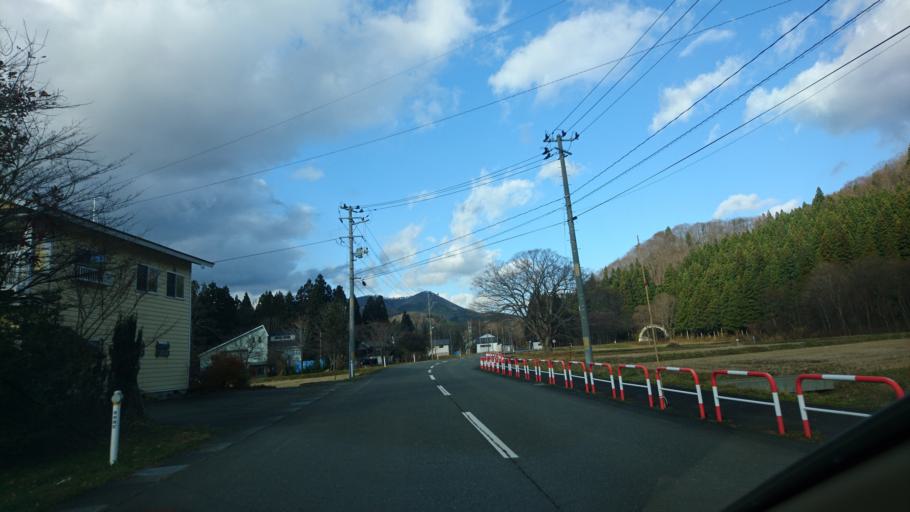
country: JP
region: Akita
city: Yokotemachi
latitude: 39.4389
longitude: 140.7582
